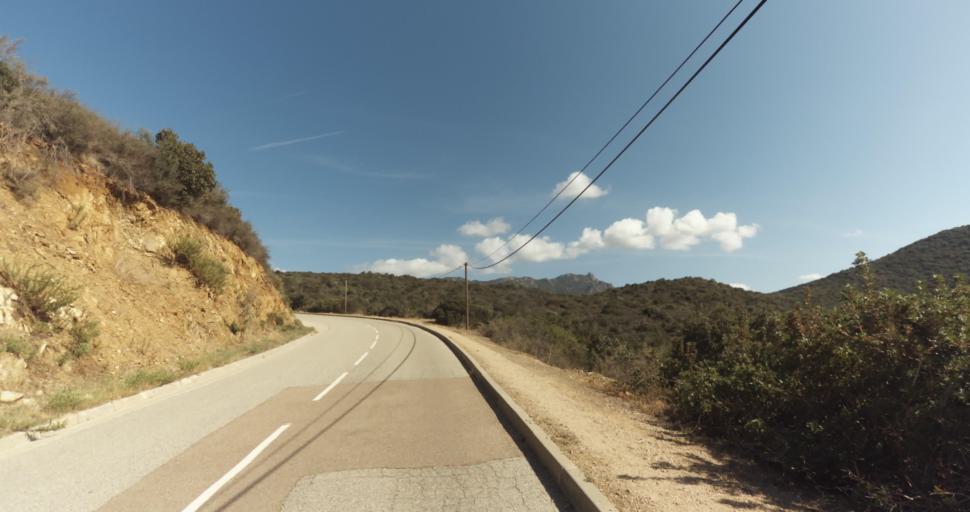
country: FR
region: Corsica
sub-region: Departement de la Corse-du-Sud
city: Ajaccio
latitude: 41.9194
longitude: 8.6434
